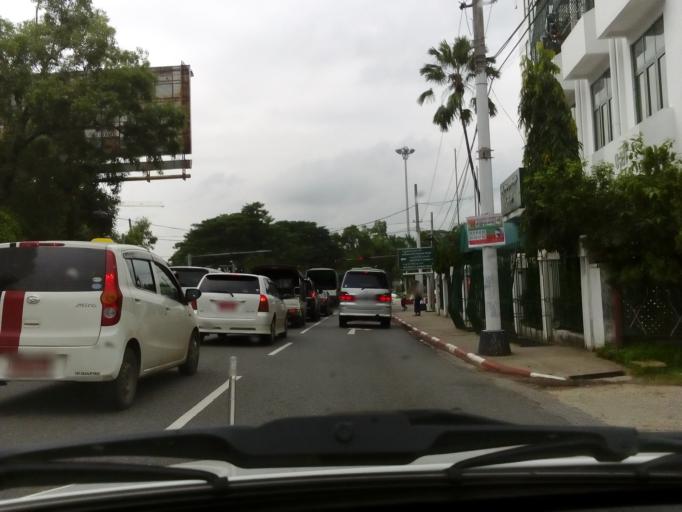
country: MM
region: Yangon
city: Yangon
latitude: 16.8226
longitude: 96.1542
